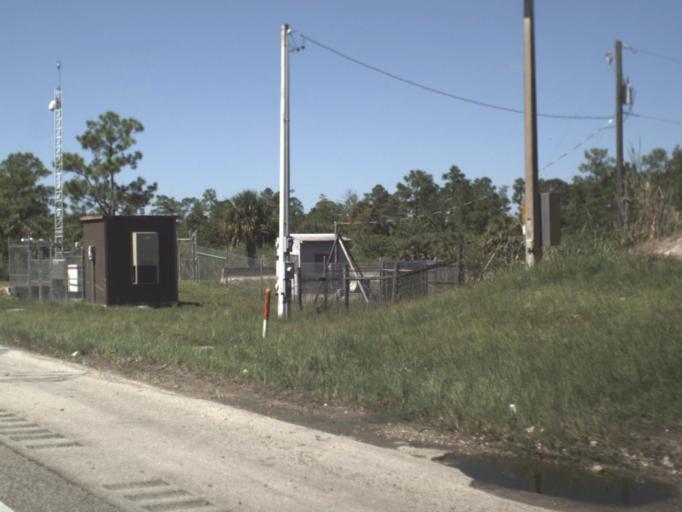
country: US
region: Florida
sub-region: Collier County
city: Orangetree
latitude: 26.1531
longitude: -81.5436
